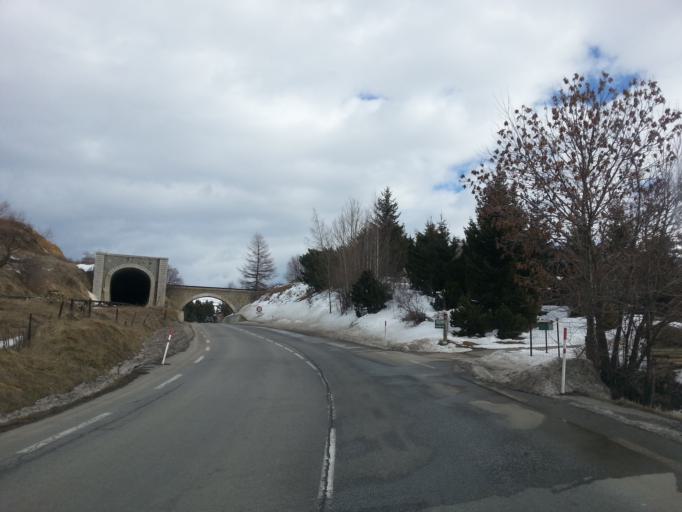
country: ES
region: Catalonia
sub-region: Provincia de Girona
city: Llivia
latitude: 42.4705
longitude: 2.0507
